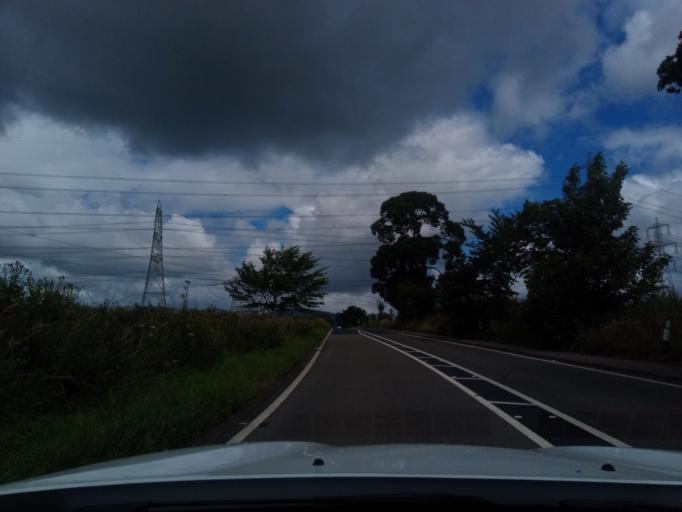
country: GB
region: Scotland
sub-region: Fife
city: Kincardine
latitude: 56.0864
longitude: -3.7195
